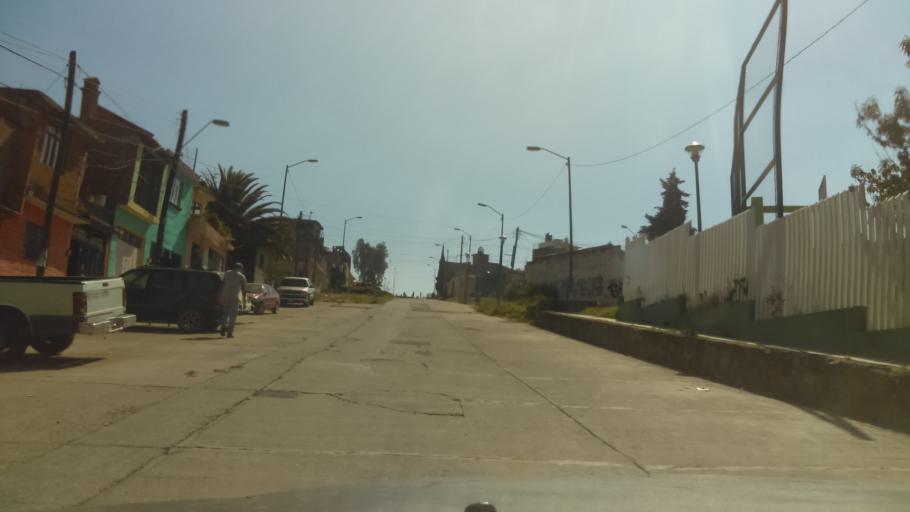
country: MX
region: Michoacan
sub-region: Morelia
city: Montana Monarca (Punta Altozano)
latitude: 19.6658
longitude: -101.1868
